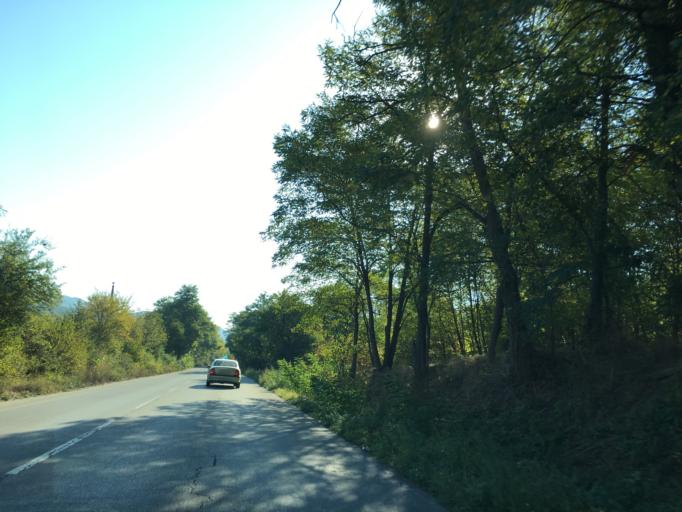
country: BG
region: Pazardzhik
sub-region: Obshtina Belovo
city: Belovo
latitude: 42.2311
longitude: 23.9556
